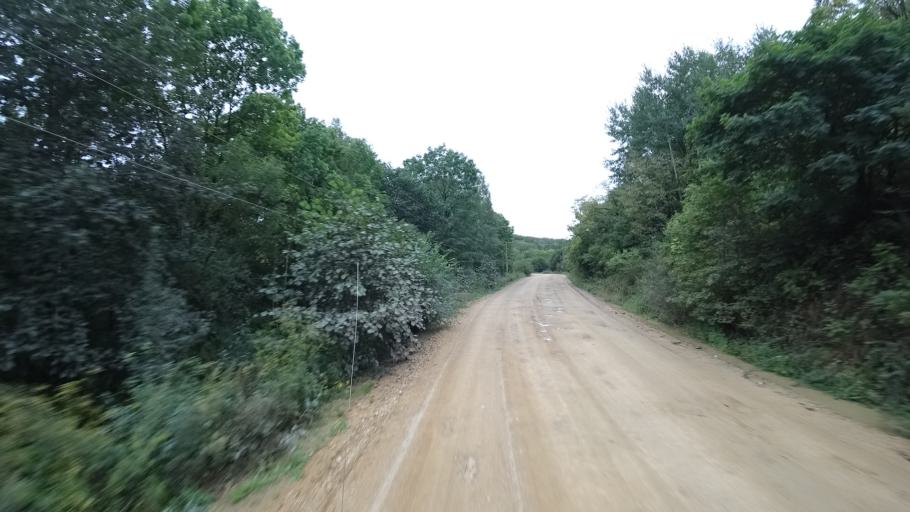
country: RU
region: Primorskiy
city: Rettikhovka
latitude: 44.1793
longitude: 132.8656
